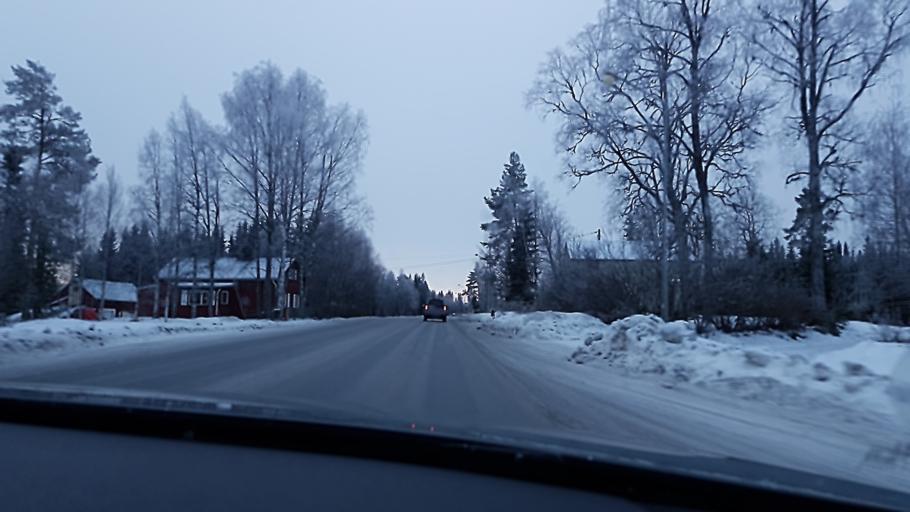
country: SE
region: Jaemtland
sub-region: OEstersunds Kommun
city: Lit
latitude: 63.2939
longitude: 14.8687
